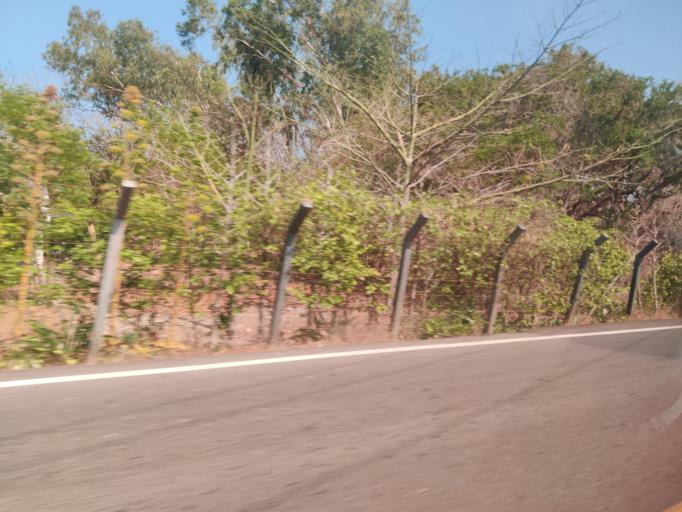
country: CO
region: Bolivar
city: Turbana
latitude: 10.1736
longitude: -75.6473
